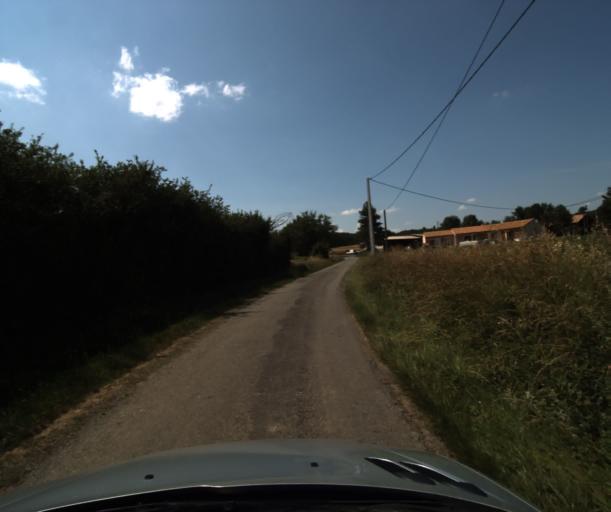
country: FR
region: Midi-Pyrenees
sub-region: Departement de la Haute-Garonne
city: Saint-Lys
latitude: 43.5291
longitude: 1.1582
